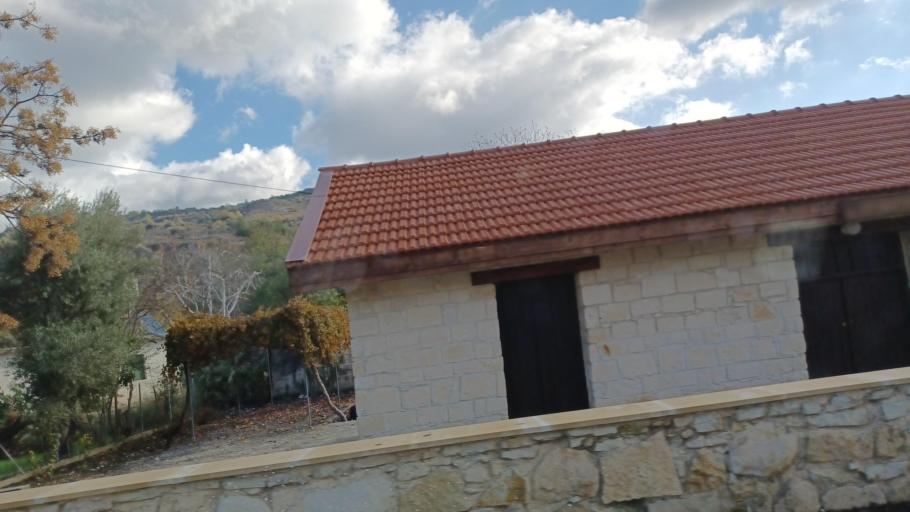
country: CY
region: Limassol
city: Pachna
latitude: 34.8665
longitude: 32.6911
